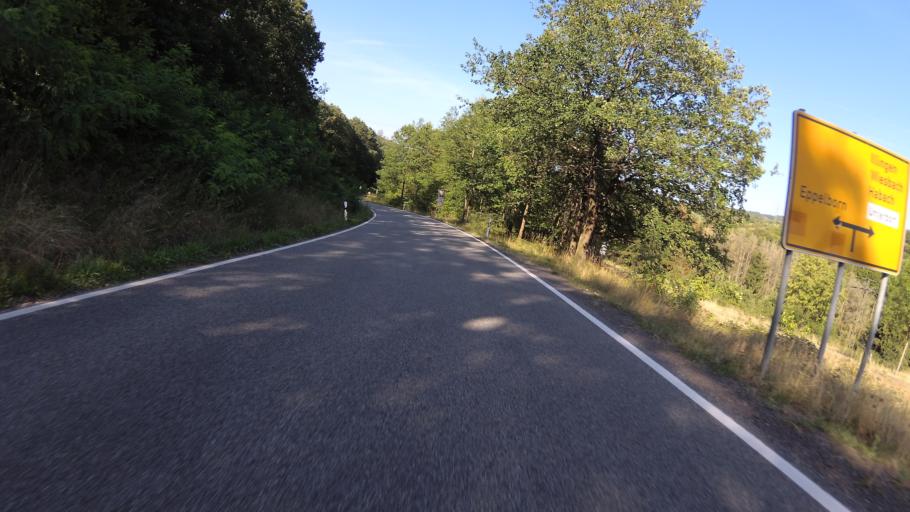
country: DE
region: Saarland
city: Eppelborn
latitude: 49.3915
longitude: 6.9599
